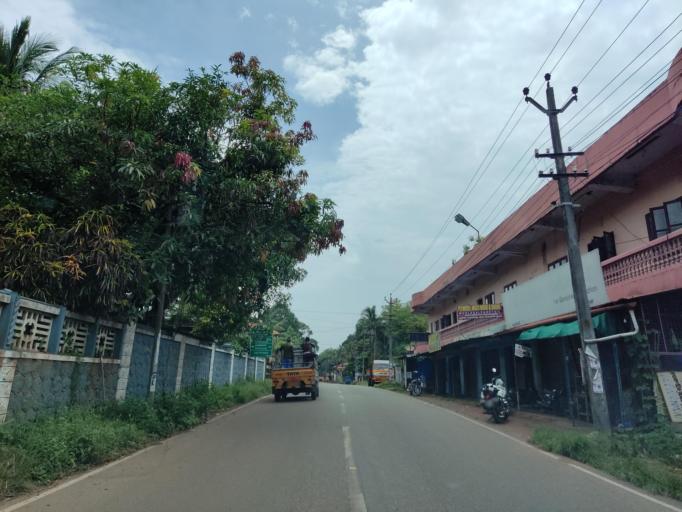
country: IN
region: Kerala
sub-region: Alappuzha
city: Mavelikara
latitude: 9.2262
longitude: 76.6156
